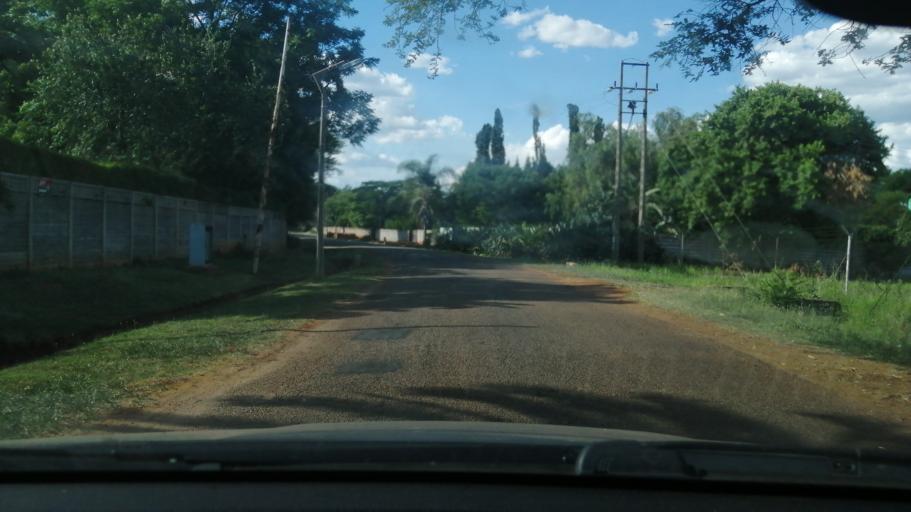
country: ZW
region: Harare
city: Harare
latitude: -17.7686
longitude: 31.0622
